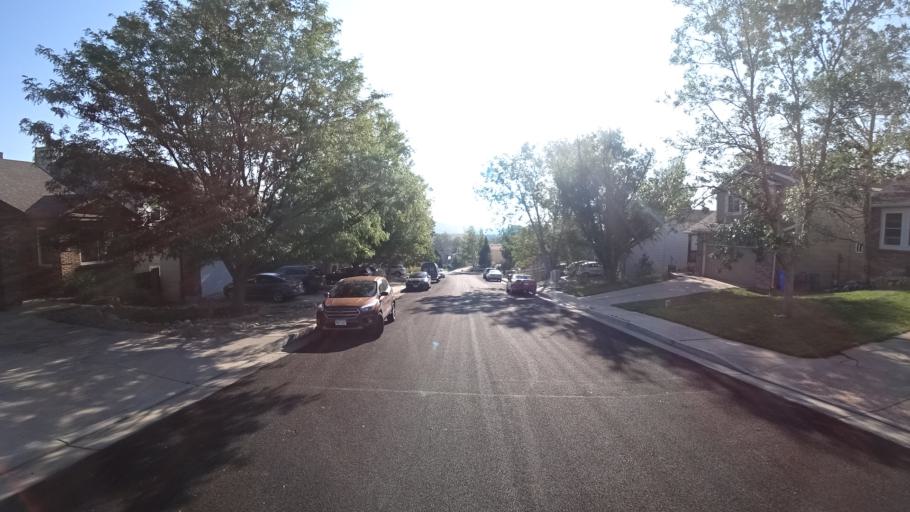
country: US
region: Colorado
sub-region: El Paso County
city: Colorado Springs
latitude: 38.8895
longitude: -104.8530
